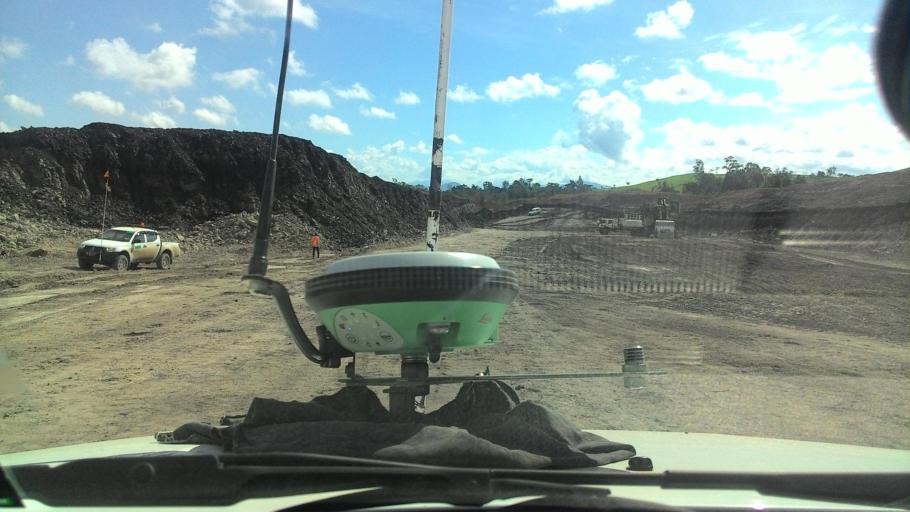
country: ID
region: South Kalimantan
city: Mungkuruyam
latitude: -2.1438
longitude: 115.5829
